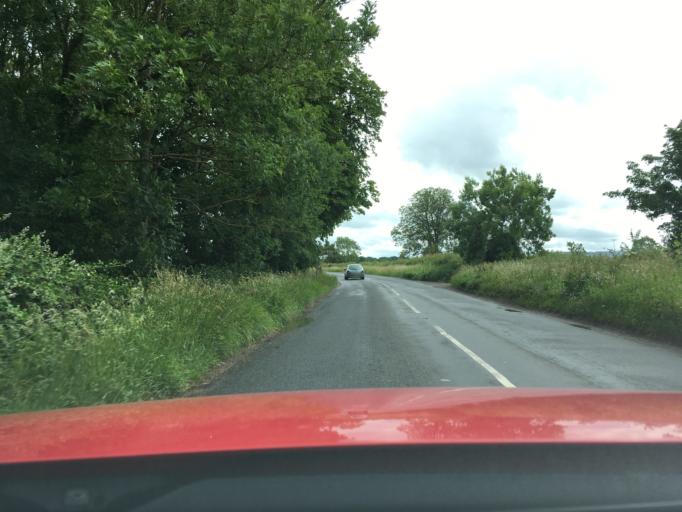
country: GB
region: England
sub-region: Worcestershire
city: Evesham
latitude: 52.0266
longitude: -1.9612
